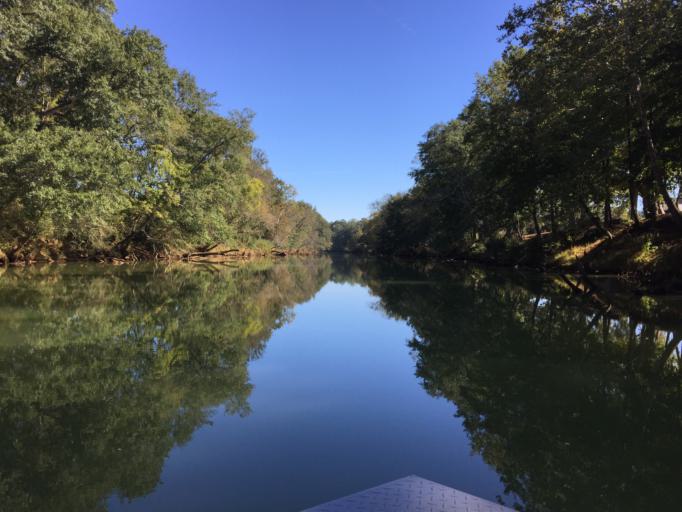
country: US
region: Georgia
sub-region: Gwinnett County
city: Berkeley Lake
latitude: 33.9919
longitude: -84.1901
